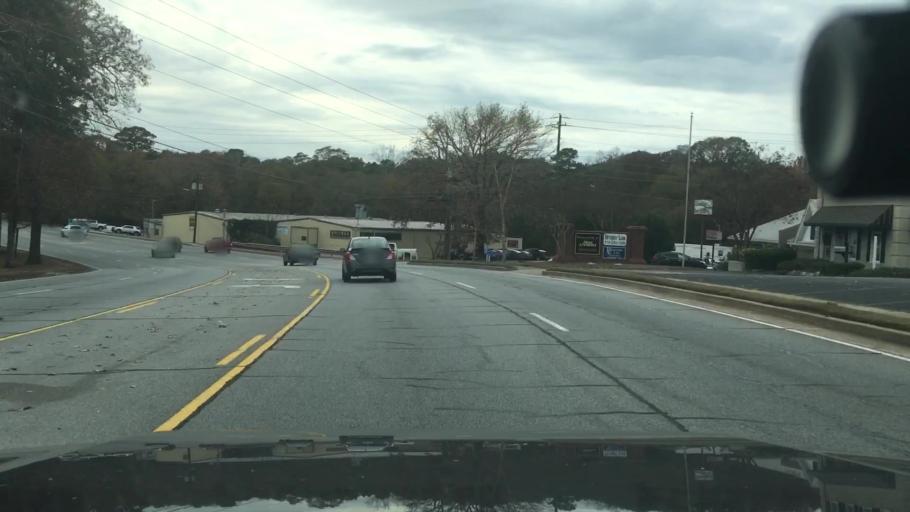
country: US
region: Georgia
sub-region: Coweta County
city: Newnan
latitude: 33.3831
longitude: -84.7921
